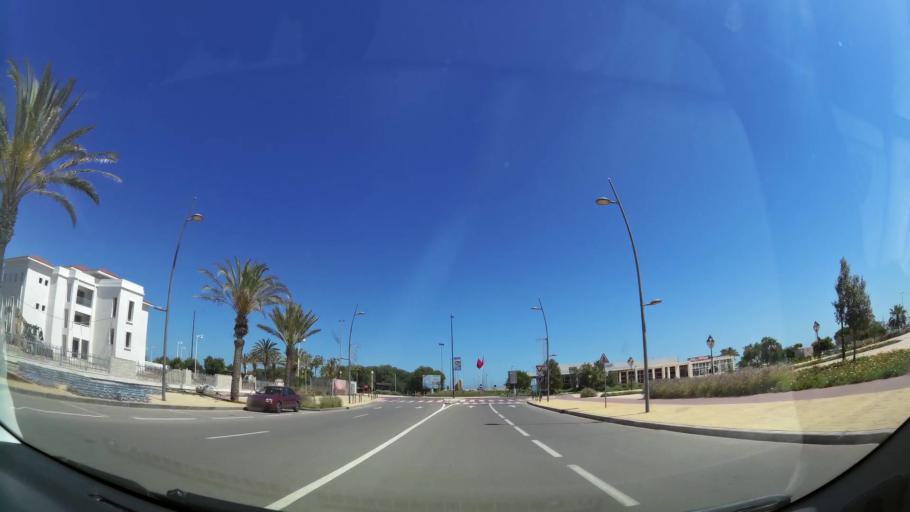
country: MA
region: Oriental
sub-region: Berkane-Taourirt
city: Madagh
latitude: 35.1087
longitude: -2.2996
